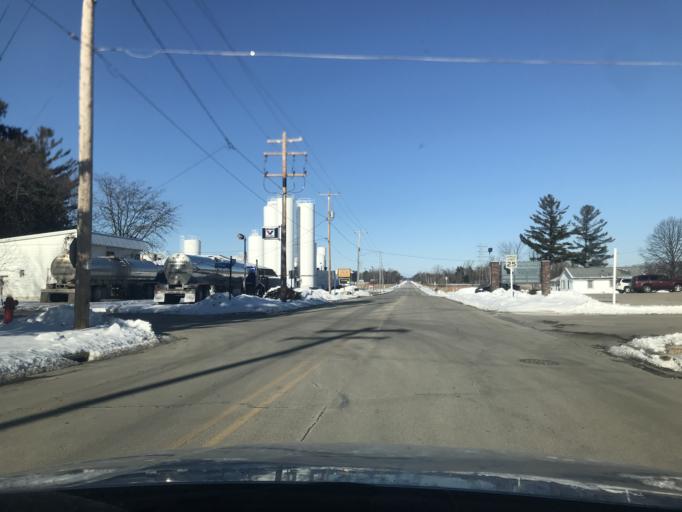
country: US
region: Wisconsin
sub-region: Oconto County
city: Oconto Falls
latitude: 44.9531
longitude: -88.0467
